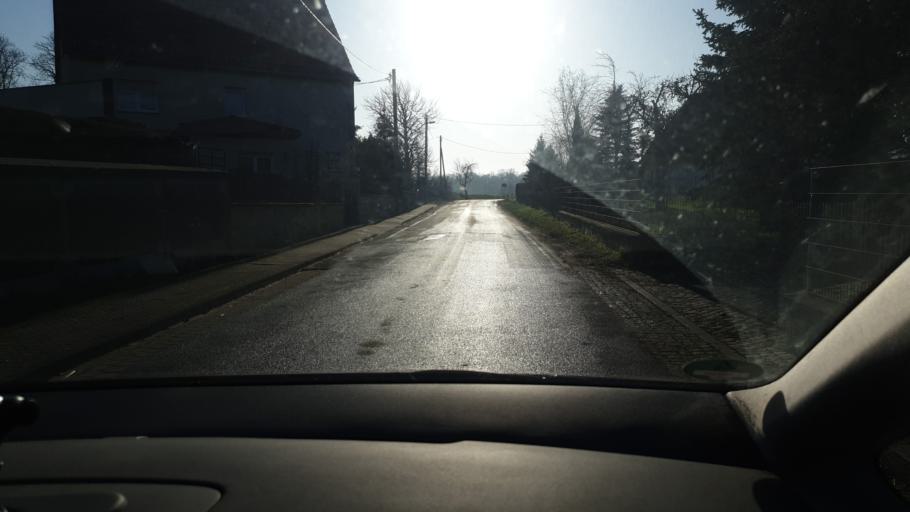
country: DE
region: Saxony
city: Hohburg
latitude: 51.4511
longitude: 12.7753
